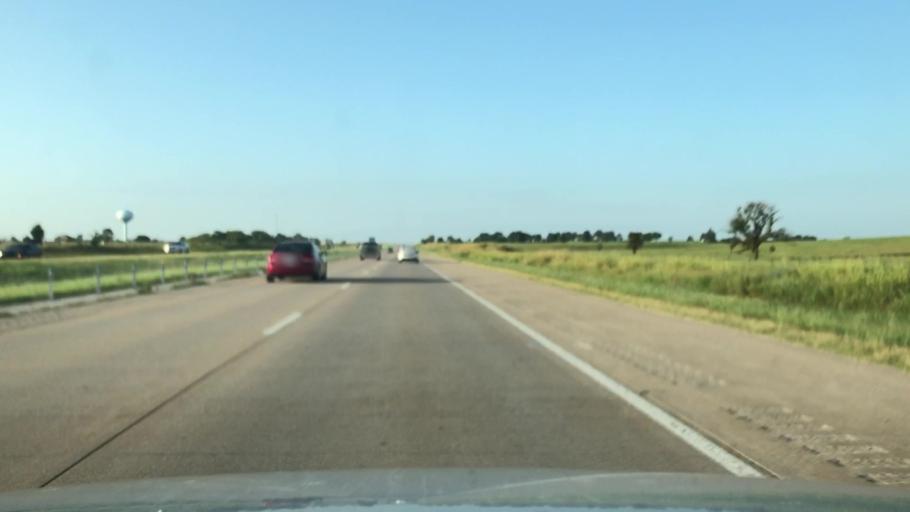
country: US
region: Oklahoma
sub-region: Washington County
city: Bartlesville
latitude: 36.6186
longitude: -95.9356
